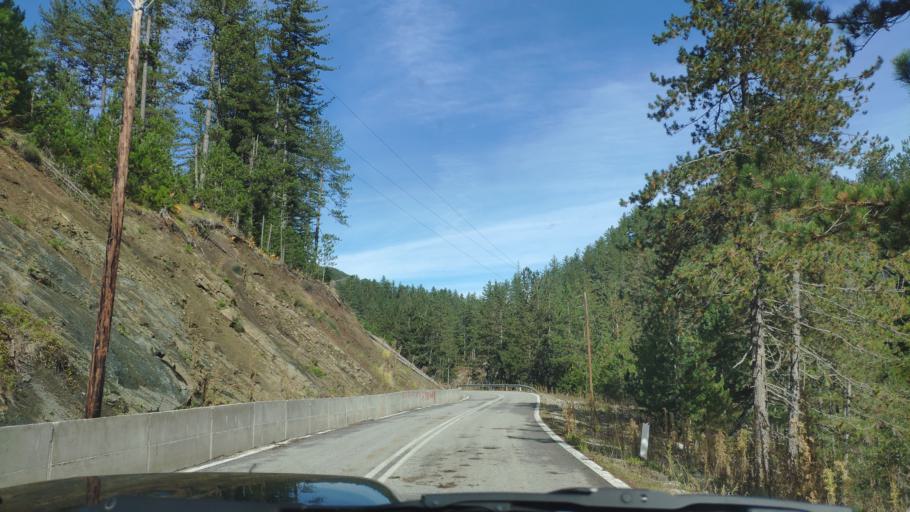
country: AL
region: Korce
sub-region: Rrethi i Devollit
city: Miras
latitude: 40.4040
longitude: 20.8794
